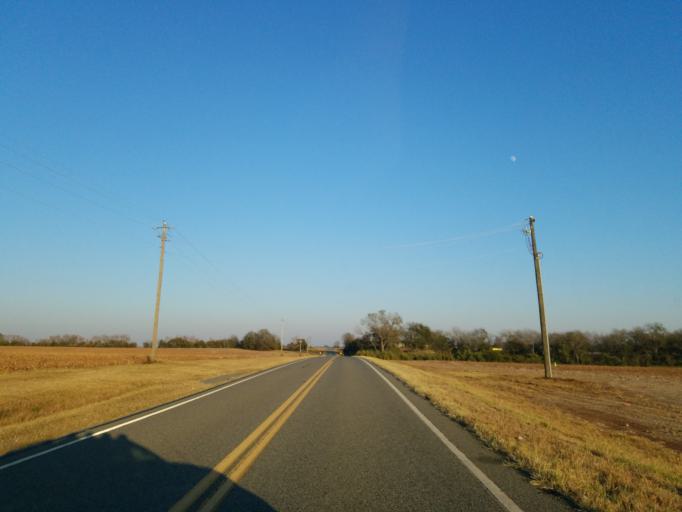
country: US
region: Georgia
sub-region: Turner County
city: Ashburn
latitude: 31.8596
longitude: -83.6058
